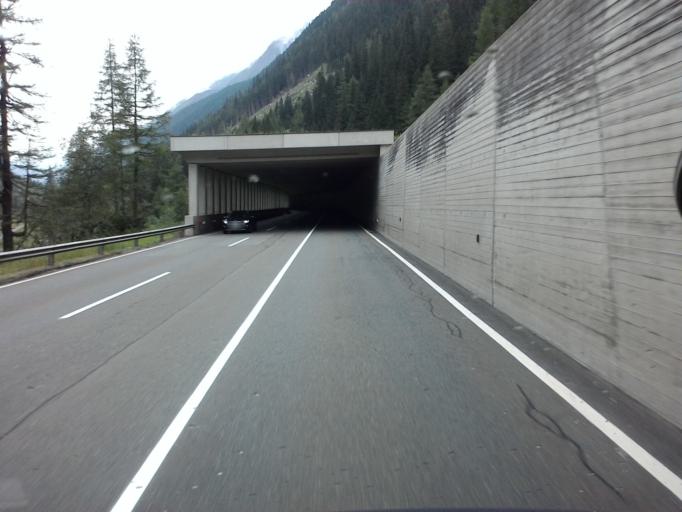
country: AT
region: Salzburg
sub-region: Politischer Bezirk Zell am See
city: Stuhlfelden
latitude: 47.1637
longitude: 12.5375
